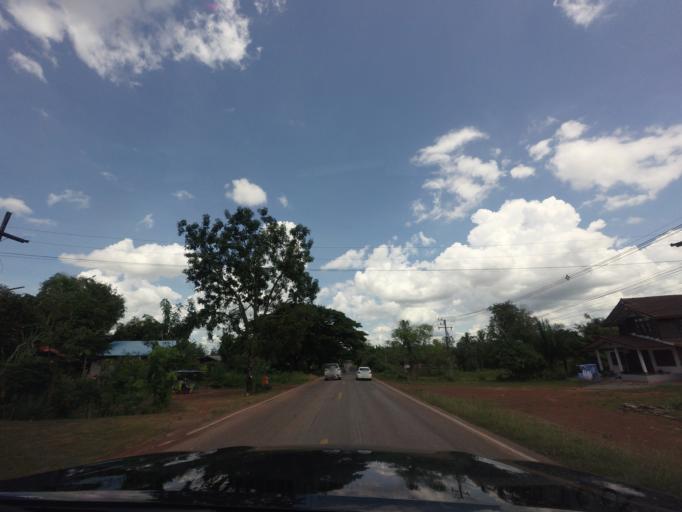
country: TH
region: Changwat Udon Thani
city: Ban Dung
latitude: 17.6547
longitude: 103.1408
